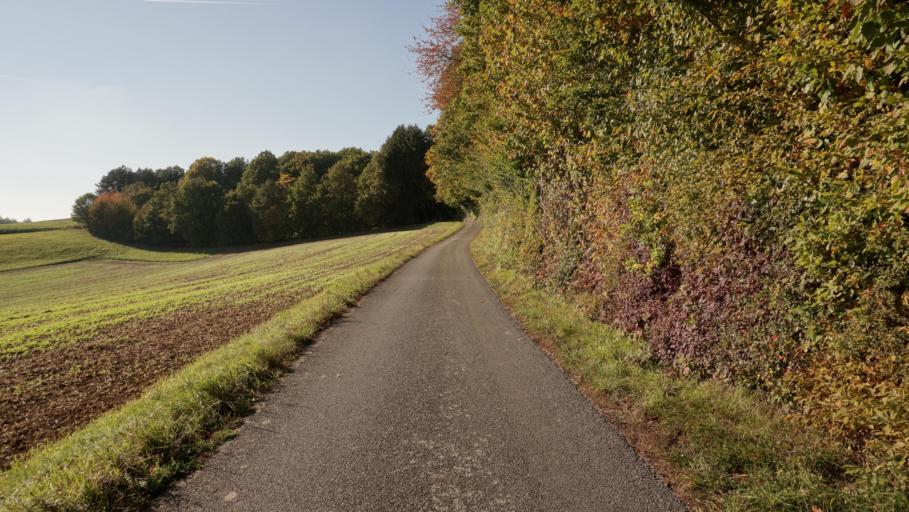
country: DE
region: Baden-Wuerttemberg
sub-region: Karlsruhe Region
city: Billigheim
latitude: 49.3596
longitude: 9.2423
